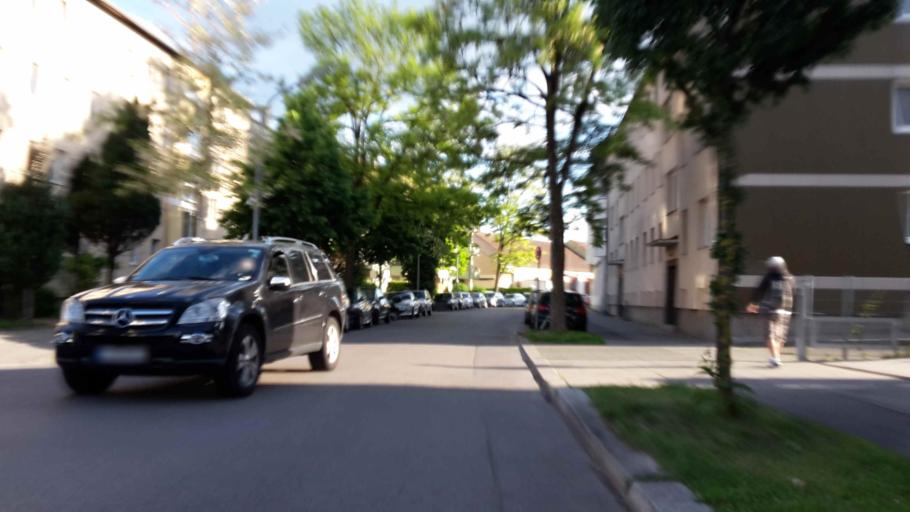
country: DE
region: Bavaria
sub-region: Upper Bavaria
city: Unterfoehring
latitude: 48.1923
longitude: 11.6178
